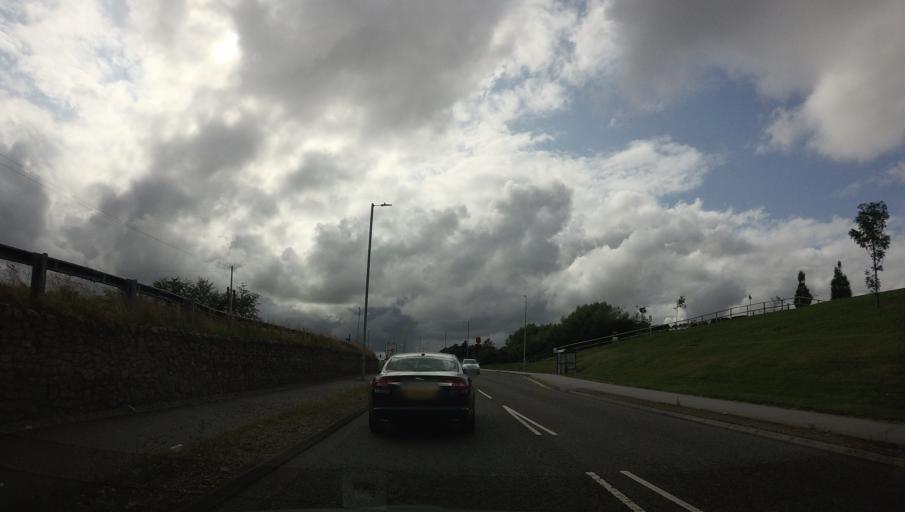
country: GB
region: Scotland
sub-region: Aberdeen City
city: Cults
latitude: 57.1503
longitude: -2.1920
